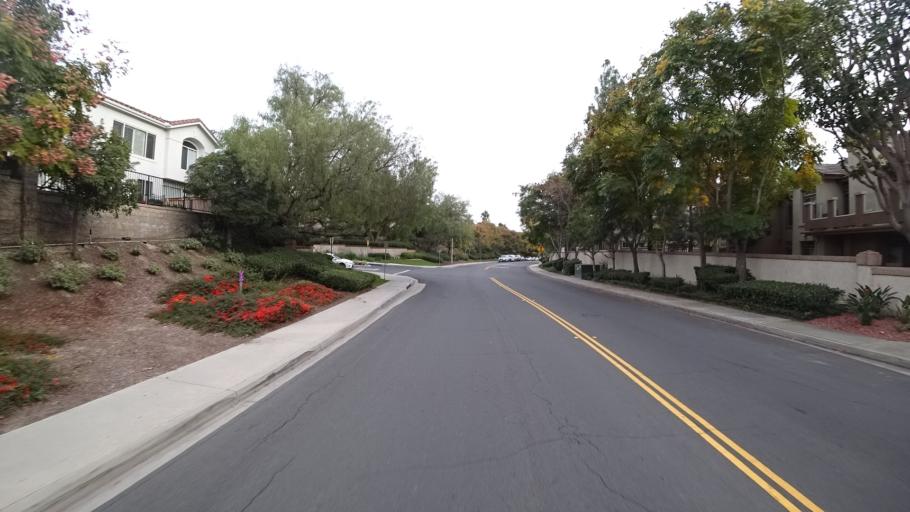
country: US
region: California
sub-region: Orange County
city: Laguna Woods
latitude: 33.5892
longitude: -117.7192
